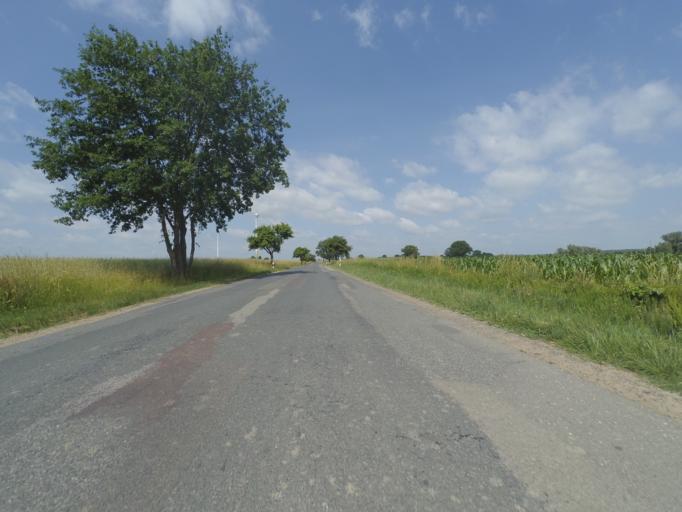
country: DE
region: Mecklenburg-Vorpommern
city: Lubz
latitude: 53.4435
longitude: 12.0112
